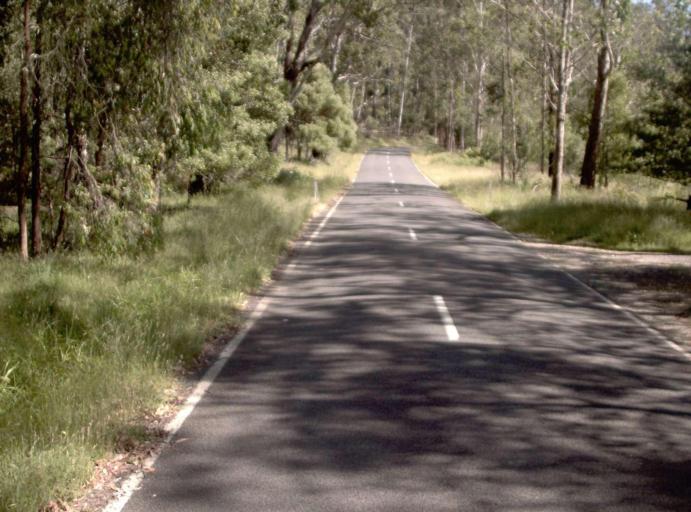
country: AU
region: New South Wales
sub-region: Bombala
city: Bombala
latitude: -37.3680
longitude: 148.6825
